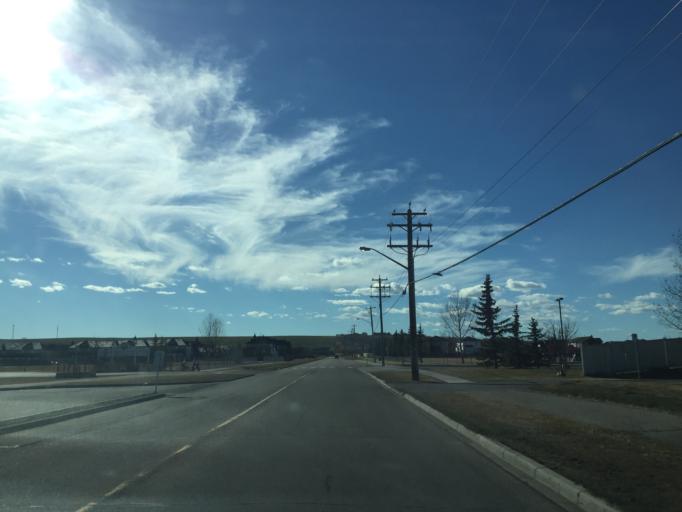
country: CA
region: Alberta
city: Airdrie
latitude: 51.2928
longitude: -114.0367
